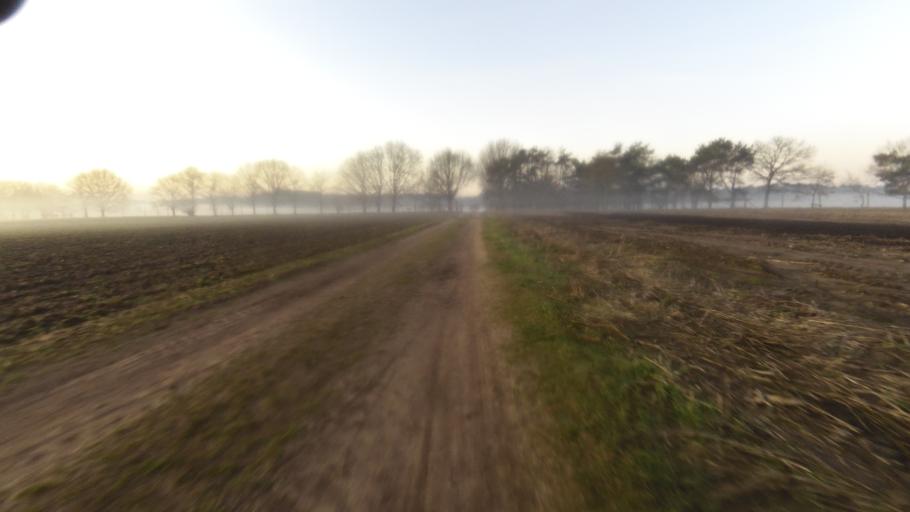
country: NL
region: Gelderland
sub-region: Gemeente Apeldoorn
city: Uddel
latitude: 52.2440
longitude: 5.7848
